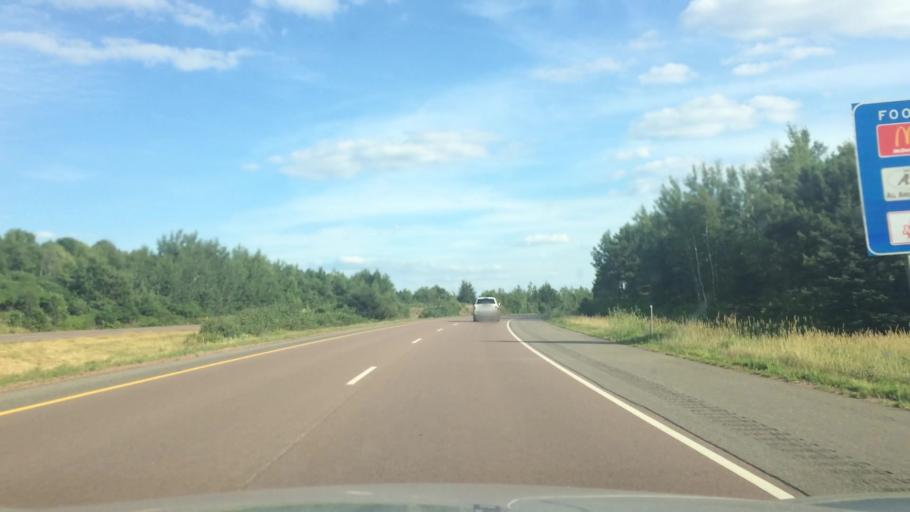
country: US
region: Wisconsin
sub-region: Marathon County
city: Wausau
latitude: 45.0087
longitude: -89.6604
